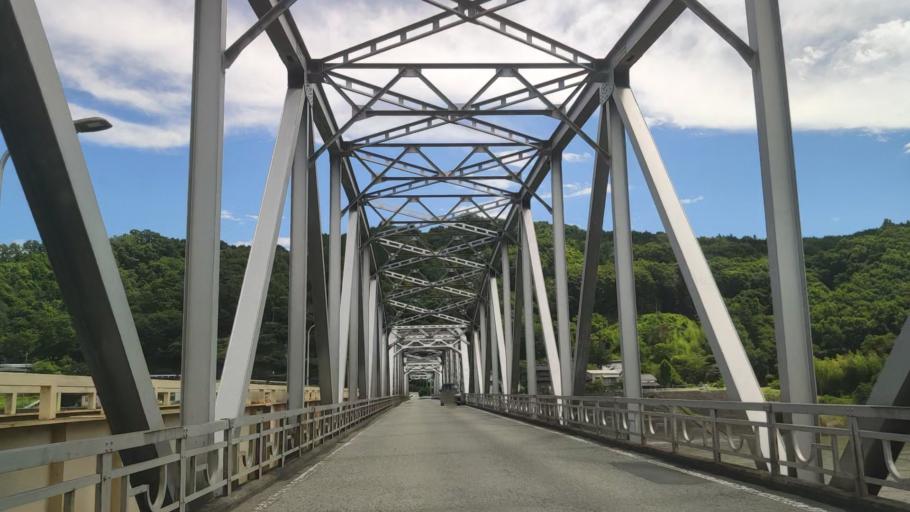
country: JP
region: Yamanashi
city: Ryuo
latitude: 35.5401
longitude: 138.4591
